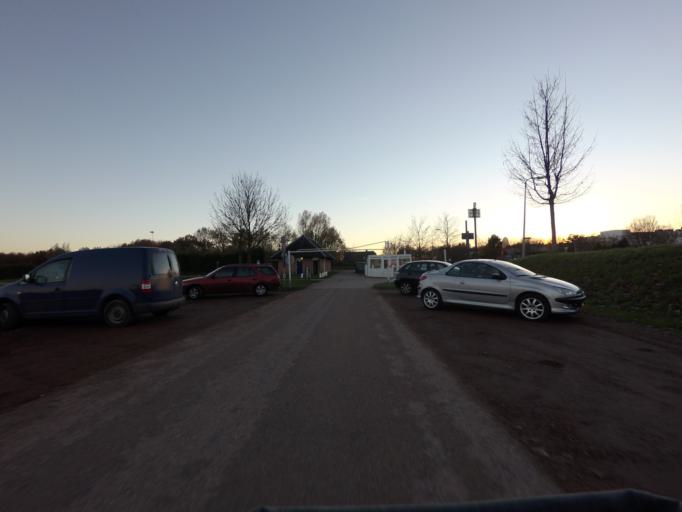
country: NL
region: Utrecht
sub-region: Gemeente Nieuwegein
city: Nieuwegein
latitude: 52.0723
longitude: 5.0553
